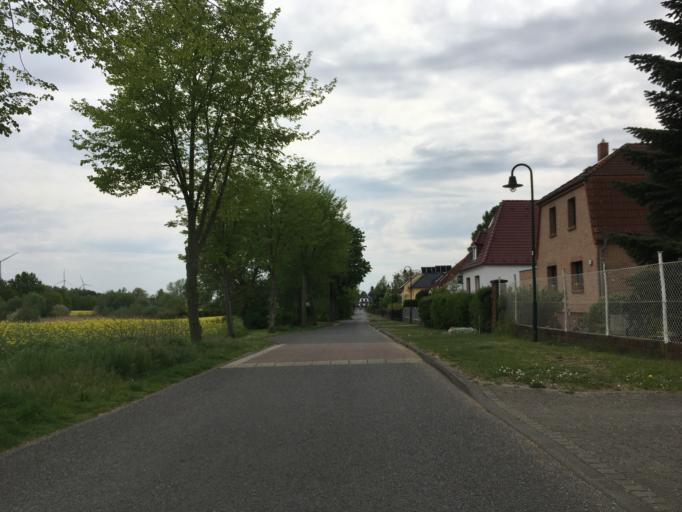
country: DE
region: Berlin
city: Buch
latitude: 52.6341
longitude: 13.5223
